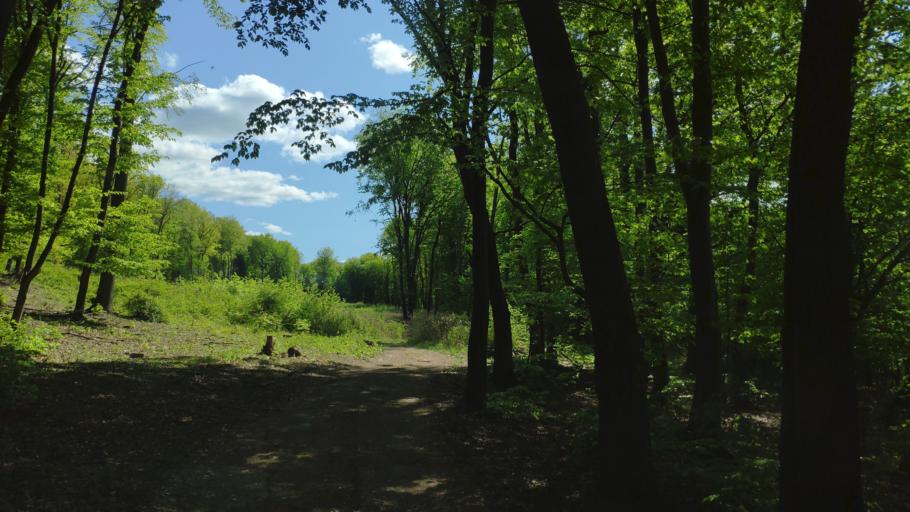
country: SK
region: Kosicky
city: Kosice
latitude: 48.6617
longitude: 21.4311
